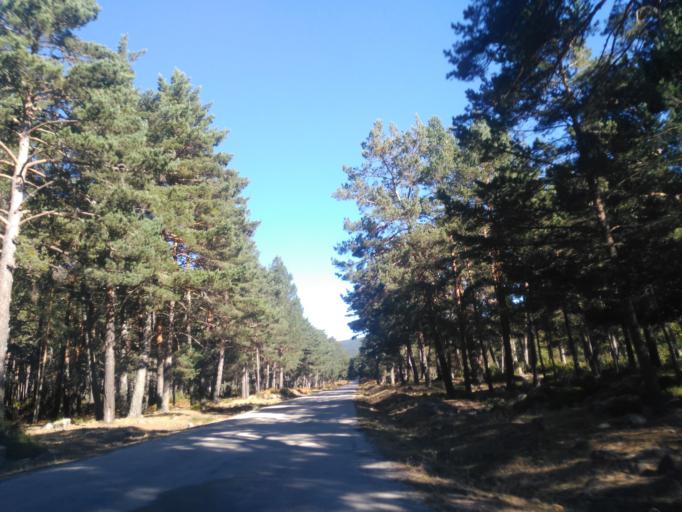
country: ES
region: Castille and Leon
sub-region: Provincia de Soria
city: Vinuesa
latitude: 41.9928
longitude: -2.8006
